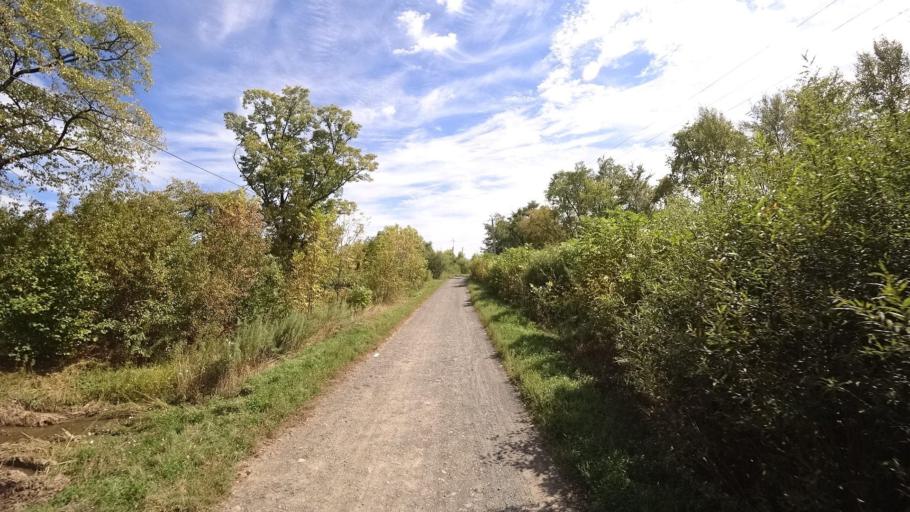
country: RU
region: Primorskiy
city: Yakovlevka
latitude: 44.6412
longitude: 133.5978
